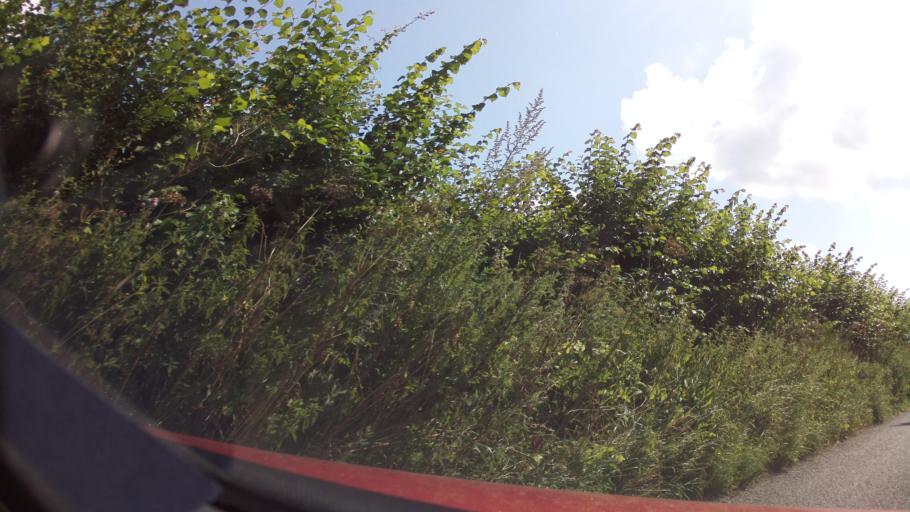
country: GB
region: England
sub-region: Wiltshire
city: Malmesbury
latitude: 51.5728
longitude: -2.0762
